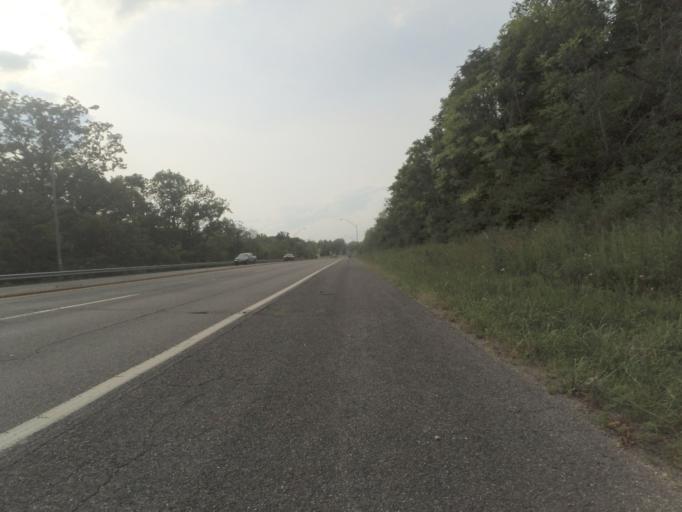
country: US
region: West Virginia
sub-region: Cabell County
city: Huntington
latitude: 38.4016
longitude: -82.4255
